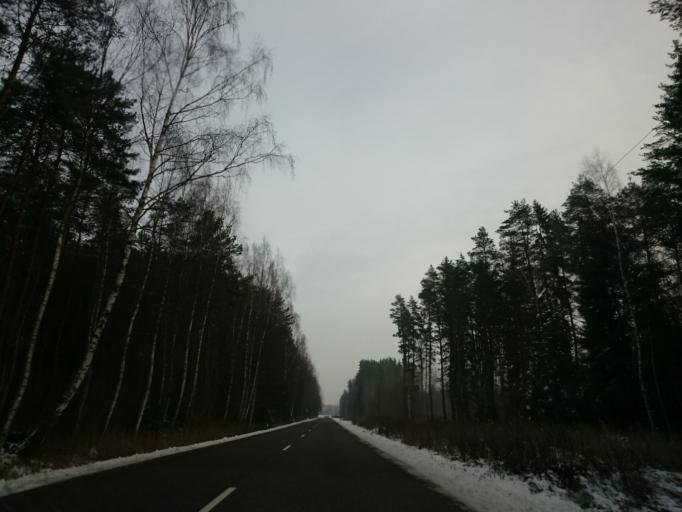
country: LV
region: Saulkrastu
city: Saulkrasti
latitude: 57.2442
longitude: 24.4891
